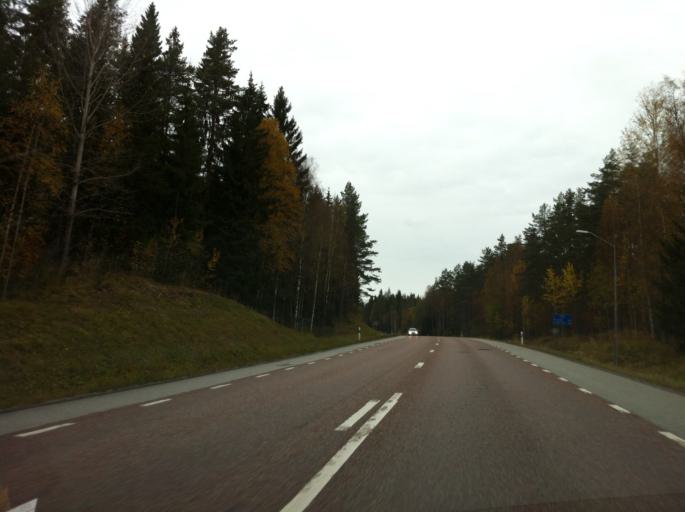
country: SE
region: Dalarna
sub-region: Ludvika Kommun
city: Grangesberg
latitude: 59.9906
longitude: 15.0183
